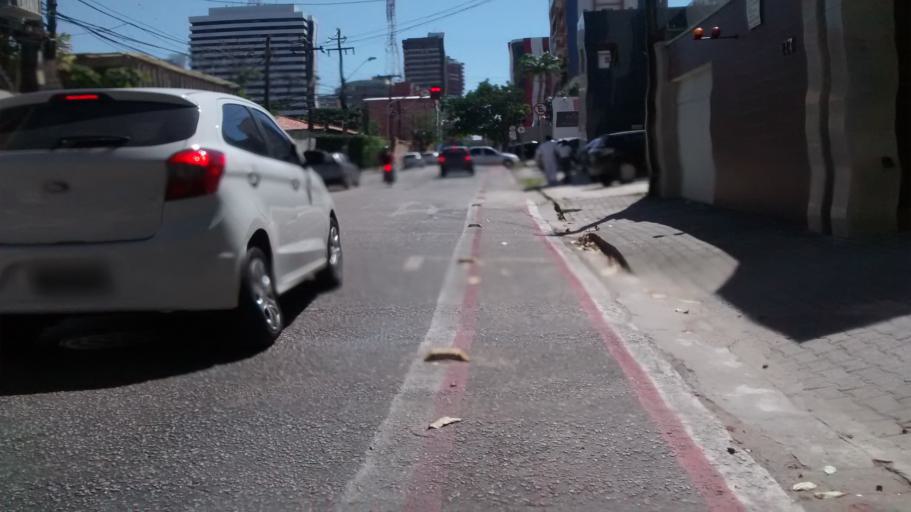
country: BR
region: Ceara
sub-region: Fortaleza
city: Fortaleza
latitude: -3.7439
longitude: -38.4981
